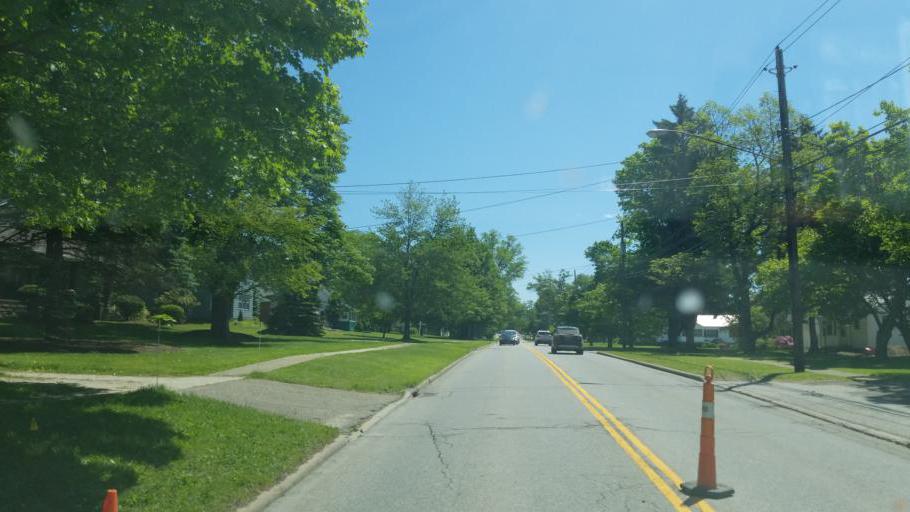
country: US
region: Ohio
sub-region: Geauga County
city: Burton
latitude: 41.4708
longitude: -81.1517
